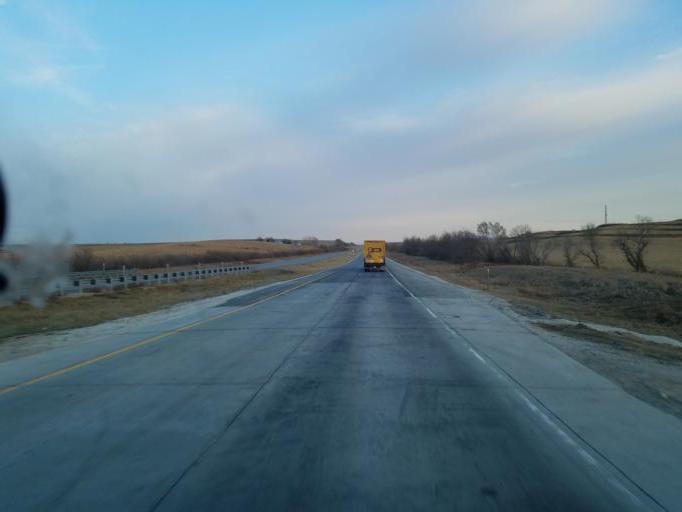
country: US
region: Iowa
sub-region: Harrison County
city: Logan
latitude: 41.4982
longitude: -95.6815
